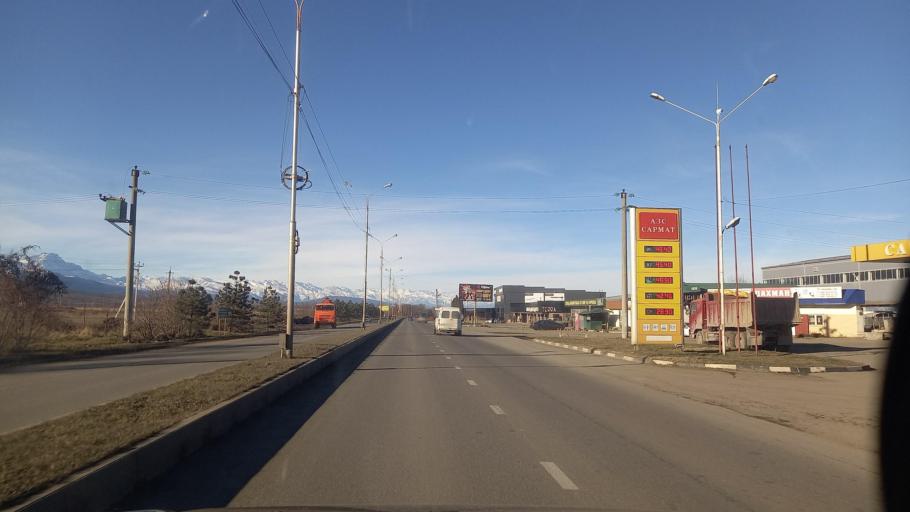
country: RU
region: North Ossetia
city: Vladikavkaz
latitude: 43.0254
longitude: 44.6332
